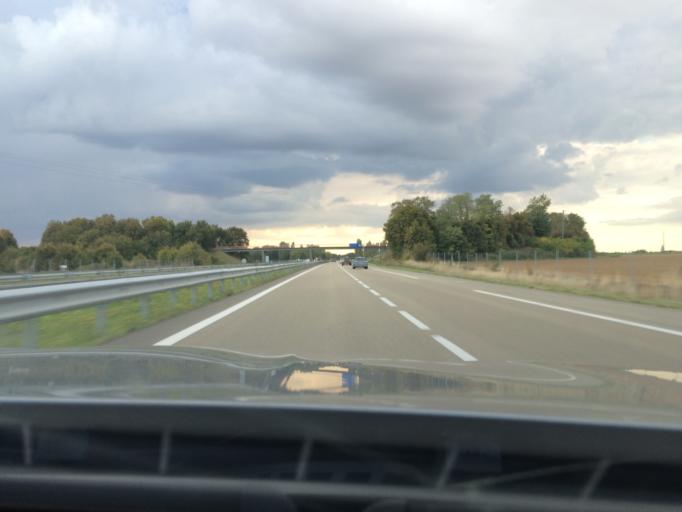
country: FR
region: Ile-de-France
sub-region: Departement de Seine-et-Marne
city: Egreville
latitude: 48.1832
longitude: 2.8345
